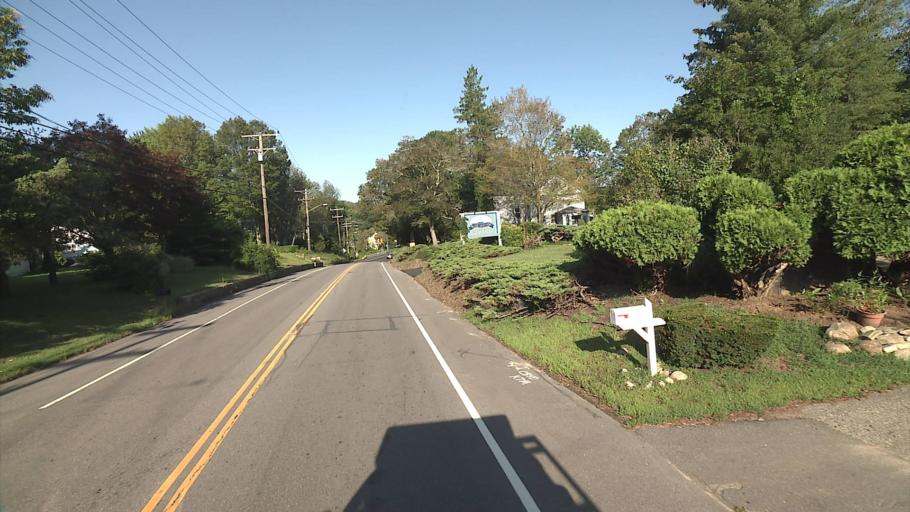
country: US
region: Connecticut
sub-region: New London County
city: Niantic
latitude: 41.3689
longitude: -72.1908
